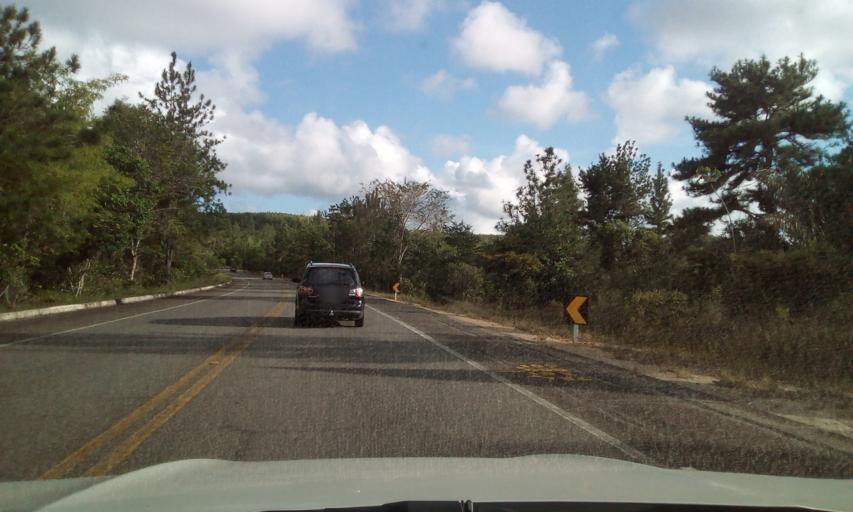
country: BR
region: Bahia
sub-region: Entre Rios
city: Entre Rios
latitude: -12.1405
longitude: -37.7916
